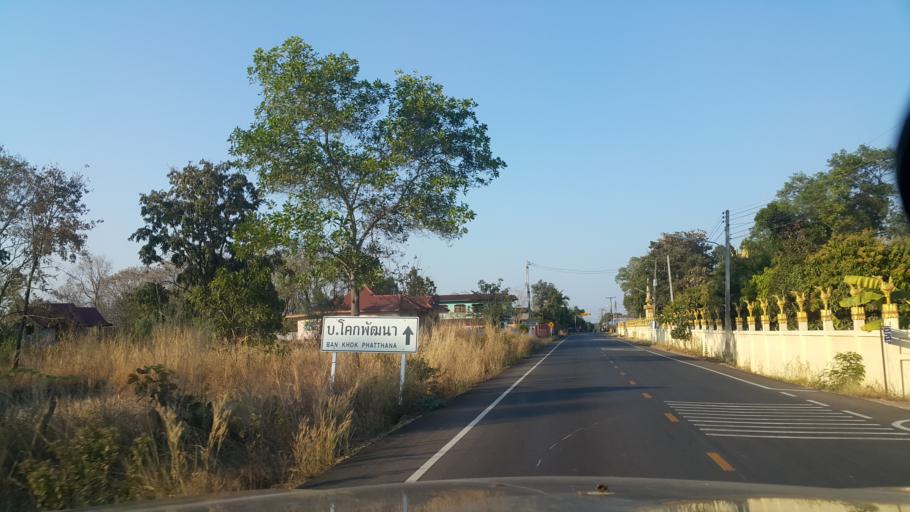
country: TH
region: Changwat Udon Thani
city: Ban Na Muang
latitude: 17.3004
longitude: 102.9452
